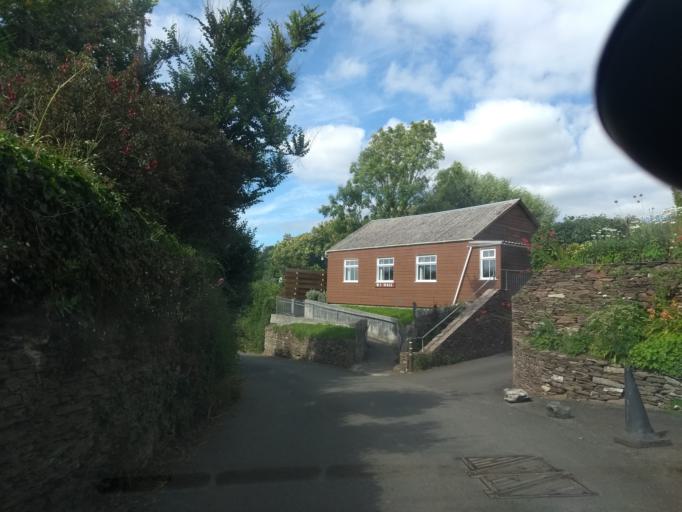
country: GB
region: England
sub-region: Devon
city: Modbury
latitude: 50.2975
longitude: -3.8930
